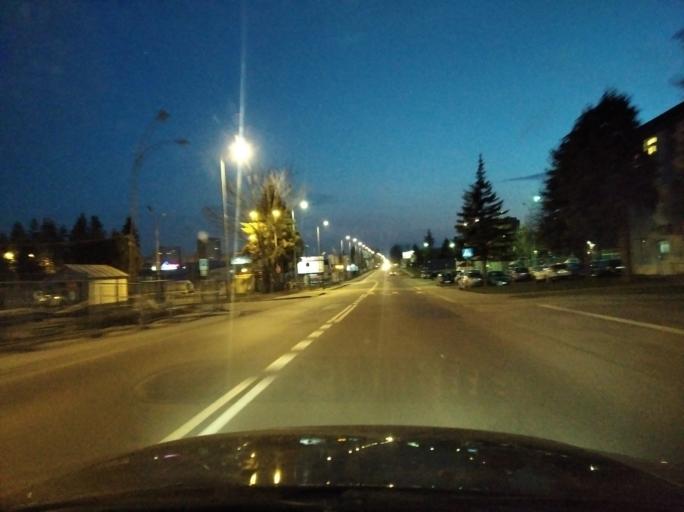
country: PL
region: Subcarpathian Voivodeship
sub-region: Rzeszow
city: Rzeszow
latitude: 50.0264
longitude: 21.9749
